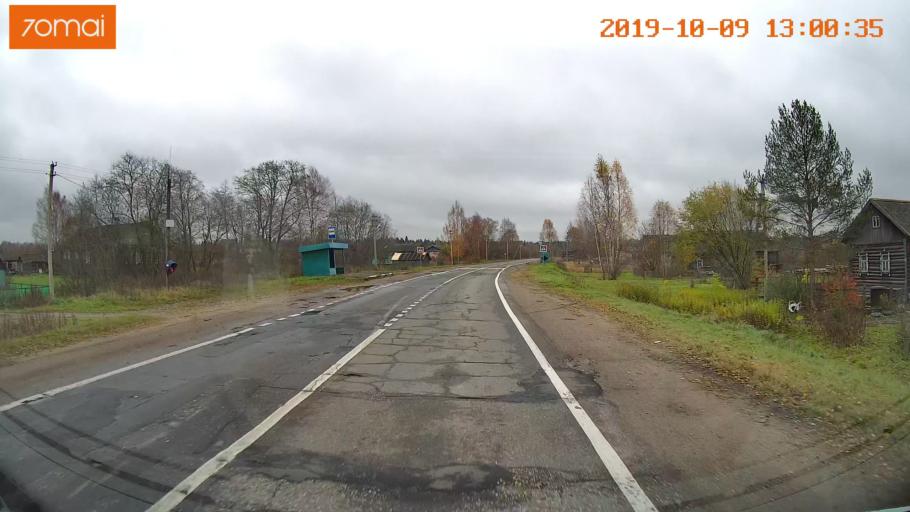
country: RU
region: Jaroslavl
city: Prechistoye
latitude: 58.3758
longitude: 40.4816
